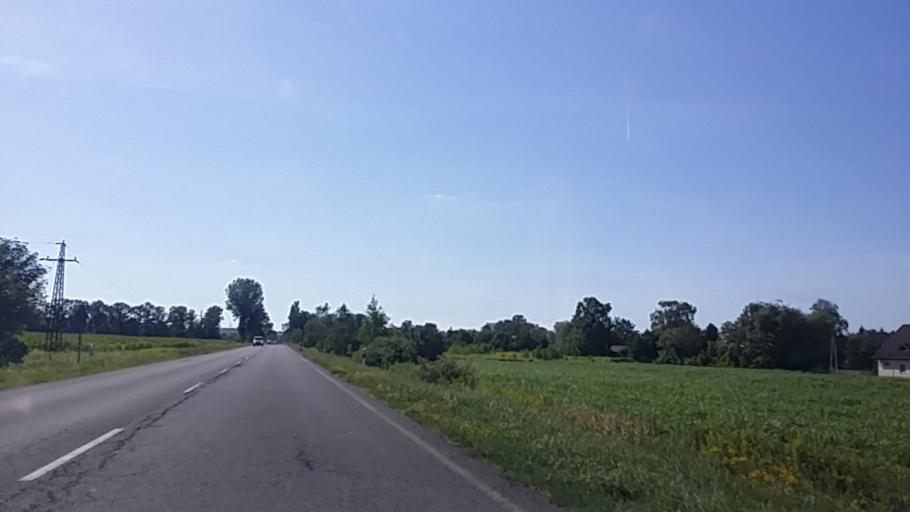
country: HU
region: Somogy
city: Kethely
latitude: 46.6981
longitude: 17.4088
